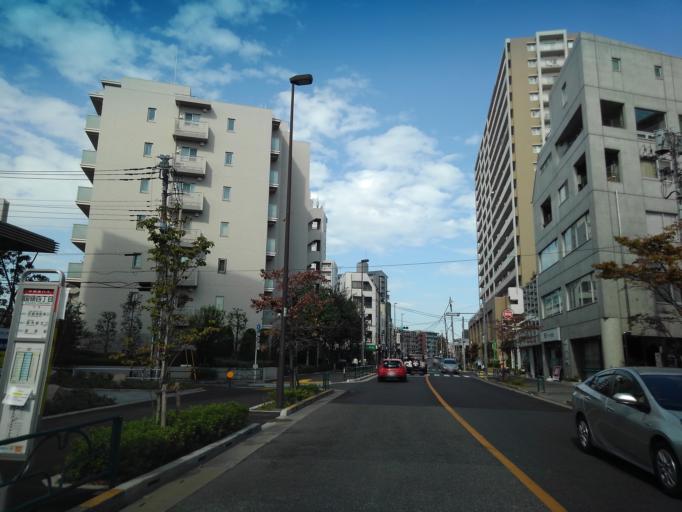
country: JP
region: Tokyo
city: Chofugaoka
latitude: 35.6484
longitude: 139.5591
